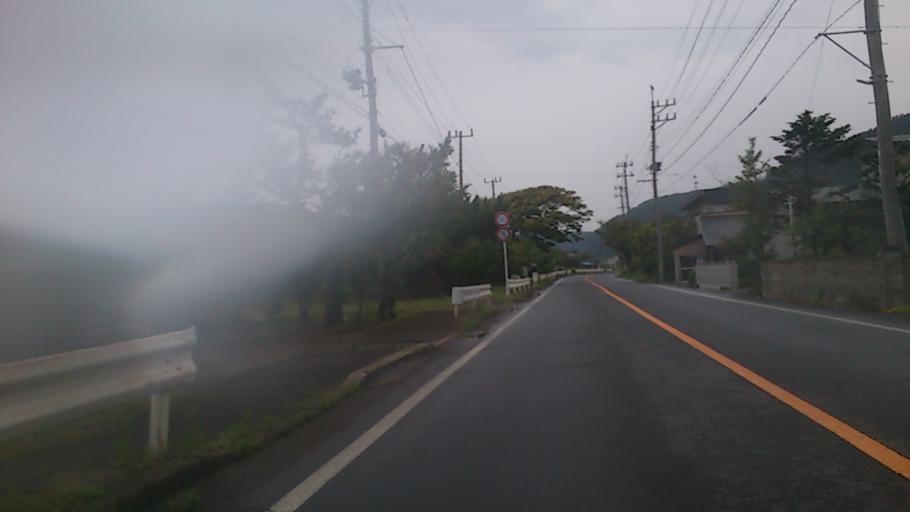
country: JP
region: Akita
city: Noshiromachi
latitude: 40.5420
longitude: 139.9461
